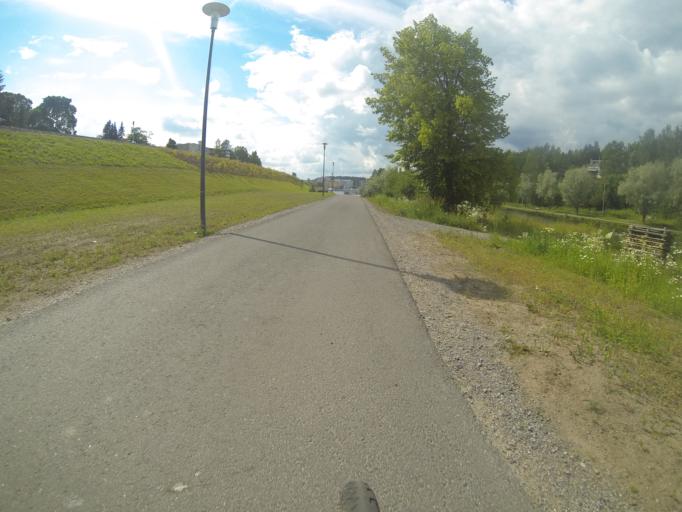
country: FI
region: Southern Savonia
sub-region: Savonlinna
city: Savonlinna
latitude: 61.8689
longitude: 28.8961
